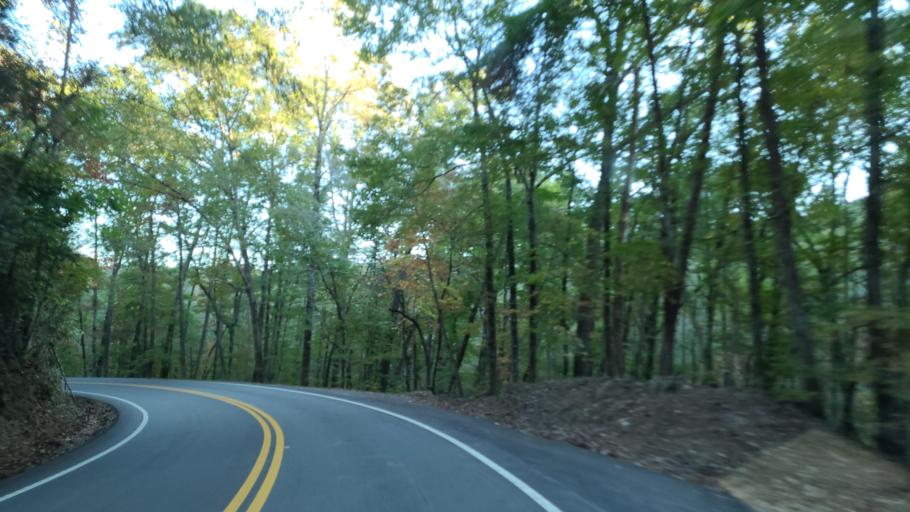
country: US
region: Georgia
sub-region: Lumpkin County
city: Dahlonega
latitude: 34.6275
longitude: -83.9518
